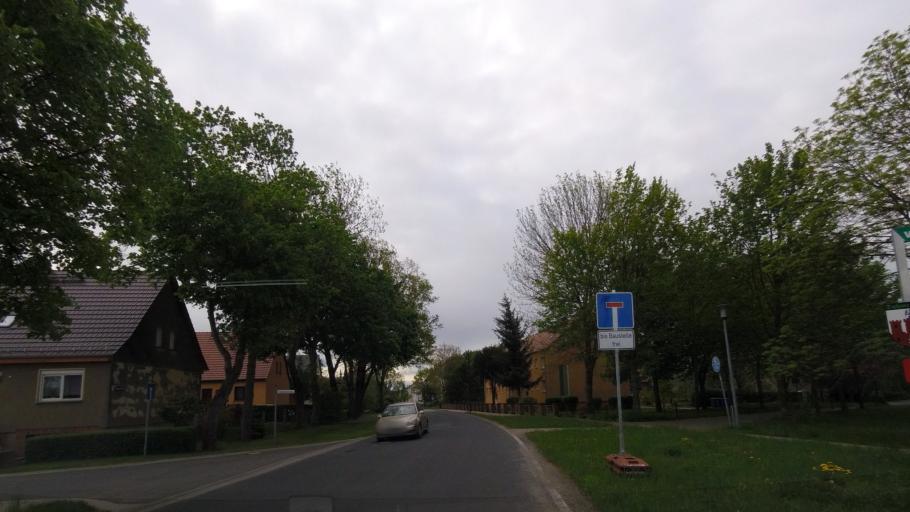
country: DE
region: Brandenburg
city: Dahme
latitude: 51.8733
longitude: 13.4214
